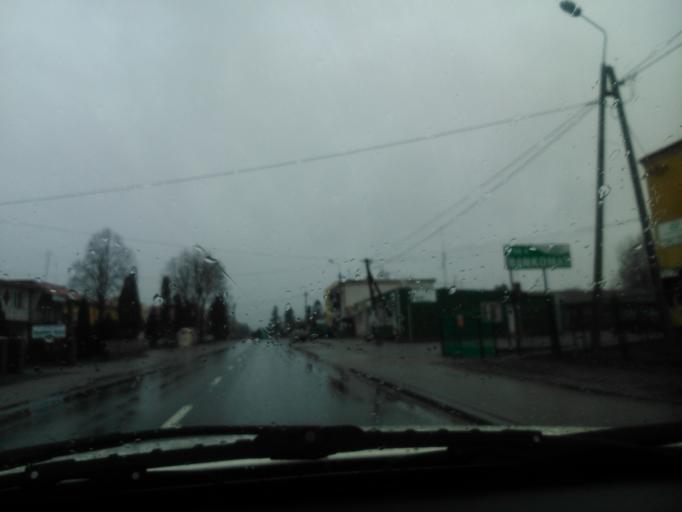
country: PL
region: Kujawsko-Pomorskie
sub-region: Powiat golubsko-dobrzynski
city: Radomin
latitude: 53.0864
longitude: 19.1971
